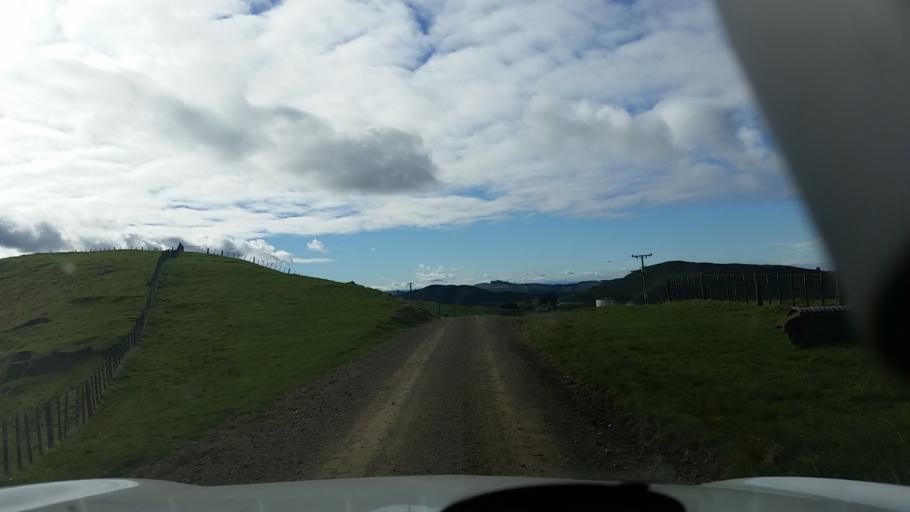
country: NZ
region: Hawke's Bay
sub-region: Napier City
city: Napier
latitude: -39.1107
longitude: 176.9363
